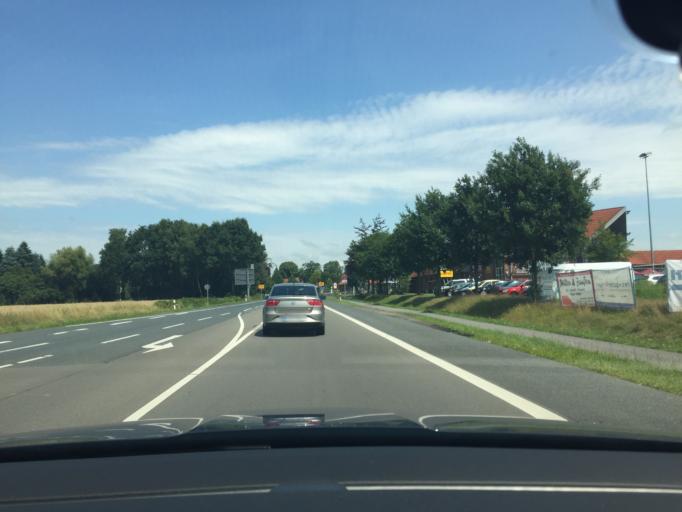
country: DE
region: Lower Saxony
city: Hesel
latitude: 53.2998
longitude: 7.5925
